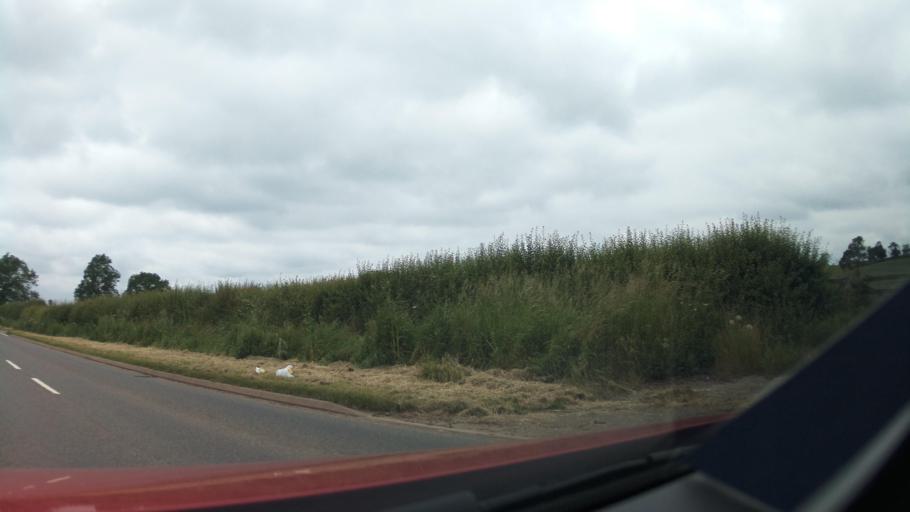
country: GB
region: England
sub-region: Leicestershire
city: Asfordby
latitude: 52.7670
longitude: -0.9666
